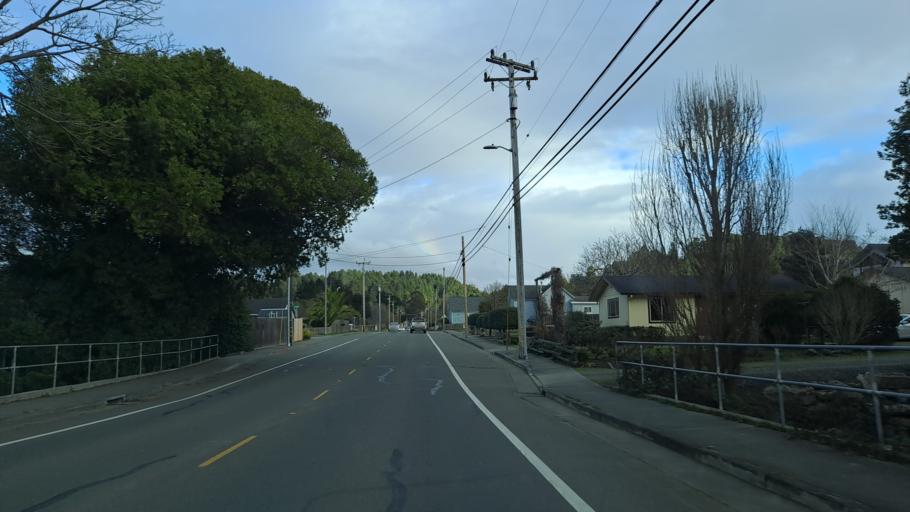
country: US
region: California
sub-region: Humboldt County
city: Fortuna
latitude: 40.5702
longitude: -124.1334
